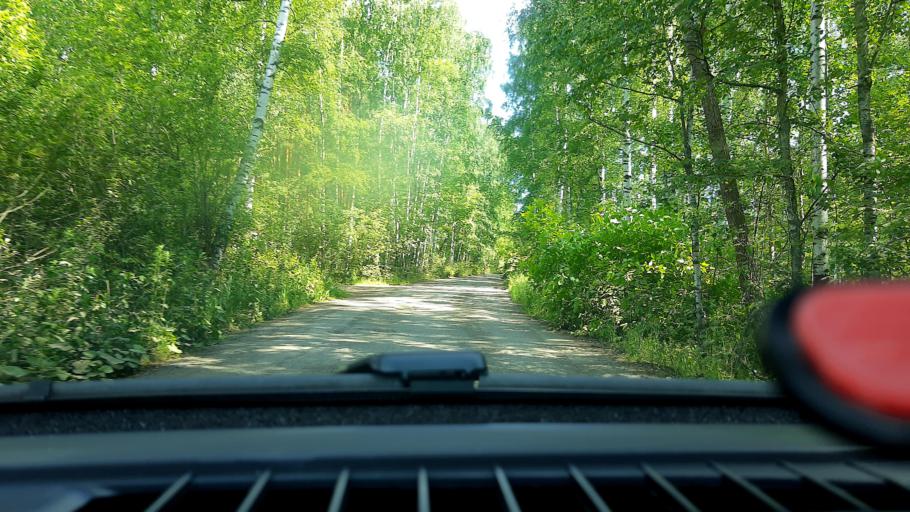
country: RU
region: Nizjnij Novgorod
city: Gorbatovka
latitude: 56.2976
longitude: 43.8197
